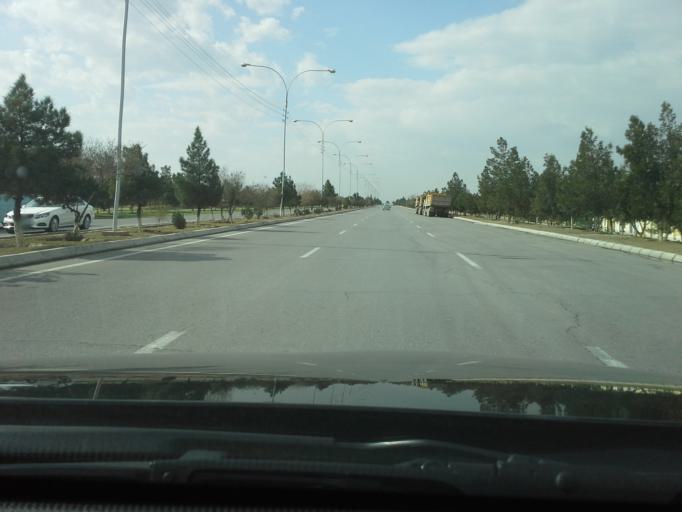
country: TM
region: Ahal
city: Ashgabat
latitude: 37.9659
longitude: 58.3055
